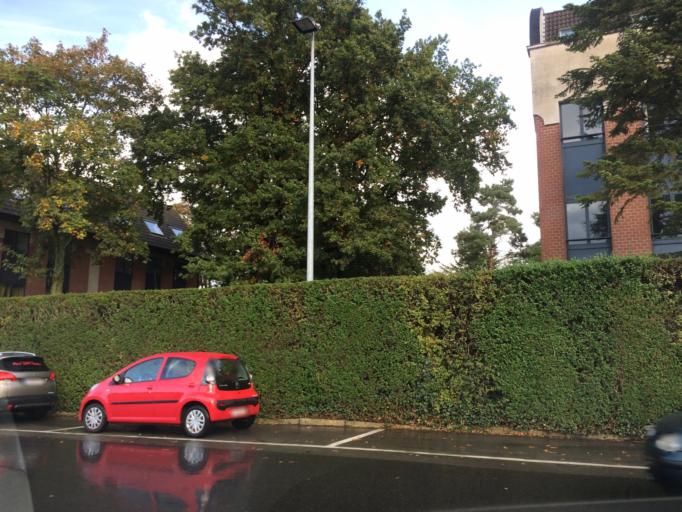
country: BE
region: Flanders
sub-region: Provincie West-Vlaanderen
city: Brugge
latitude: 51.2005
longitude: 3.1912
